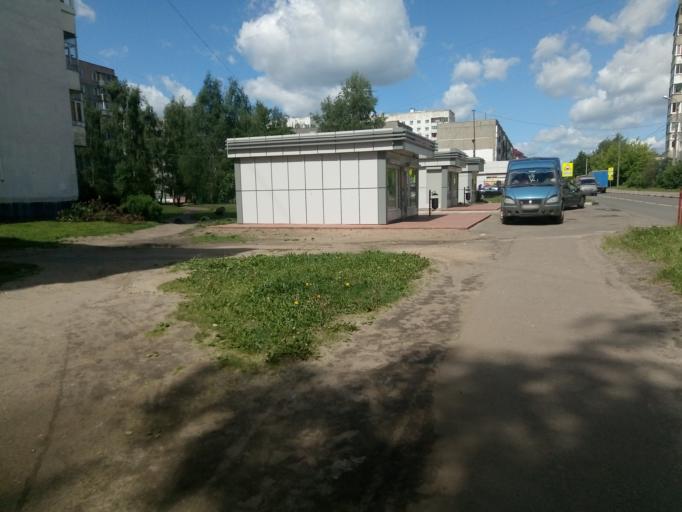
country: RU
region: Jaroslavl
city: Yaroslavl
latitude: 57.6557
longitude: 39.9588
